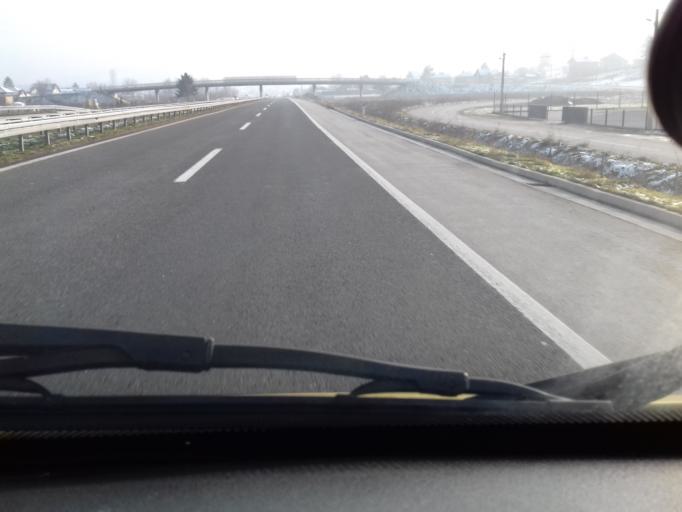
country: BA
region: Federation of Bosnia and Herzegovina
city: Gornje Mostre
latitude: 44.0198
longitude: 18.1359
